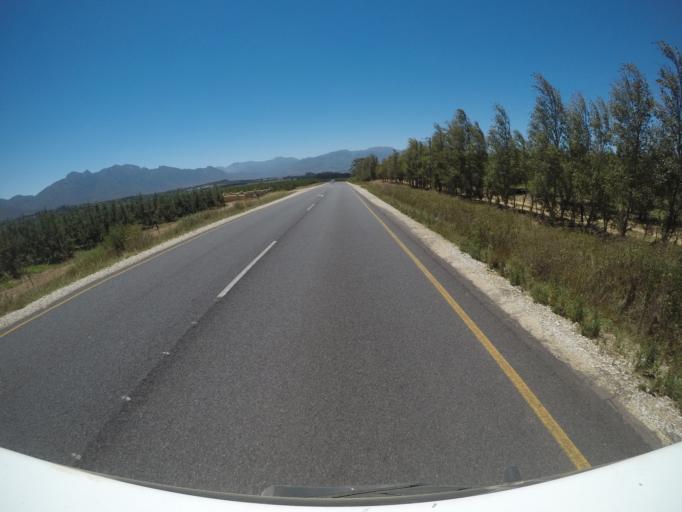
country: ZA
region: Western Cape
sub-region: Overberg District Municipality
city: Grabouw
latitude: -34.0621
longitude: 19.1350
